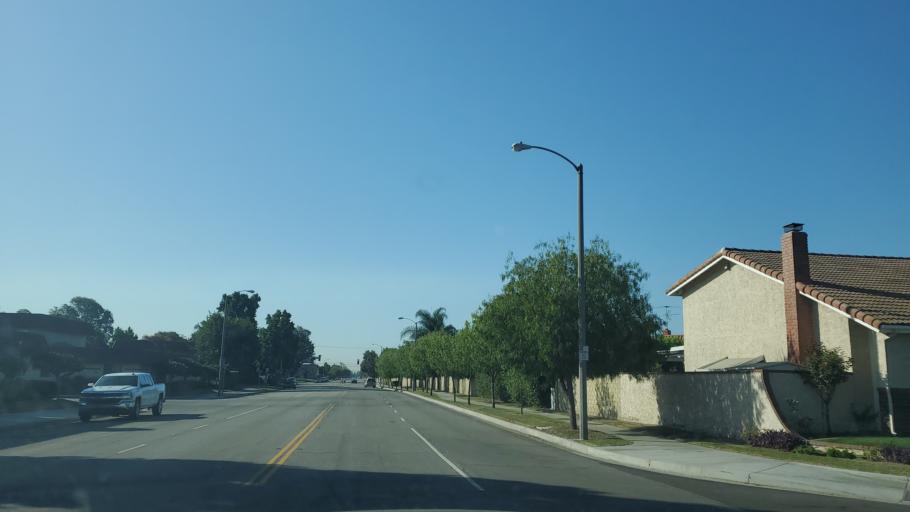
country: US
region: California
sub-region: Orange County
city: Cypress
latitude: 33.7977
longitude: -118.0198
